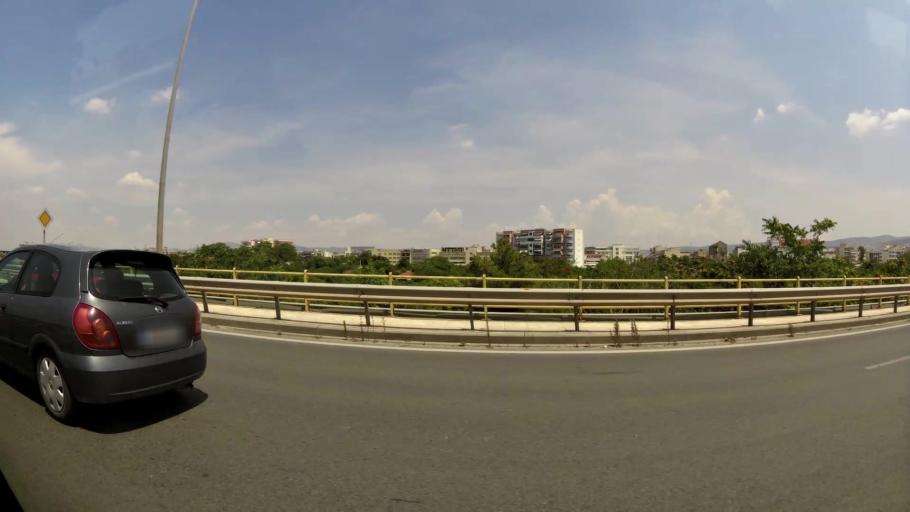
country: GR
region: Central Macedonia
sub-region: Nomos Thessalonikis
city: Ampelokipoi
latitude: 40.6482
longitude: 22.9123
